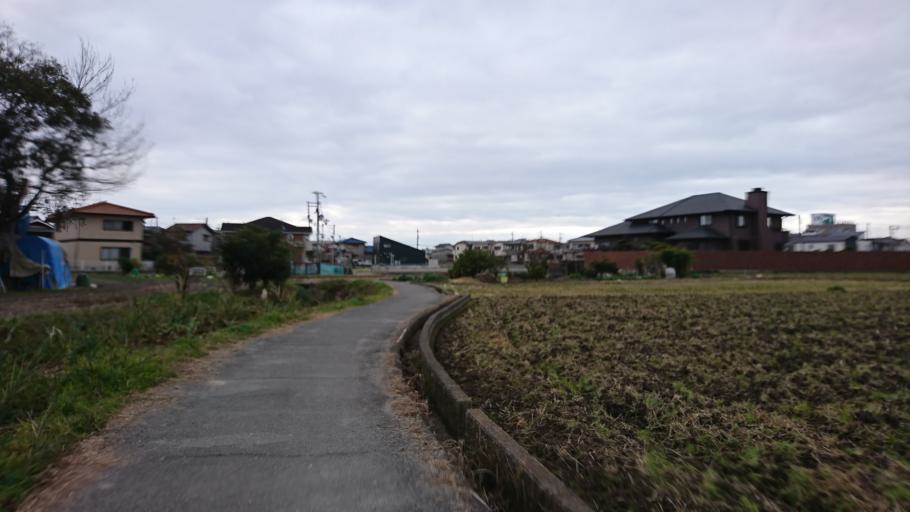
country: JP
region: Hyogo
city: Kakogawacho-honmachi
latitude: 34.7456
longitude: 134.8553
